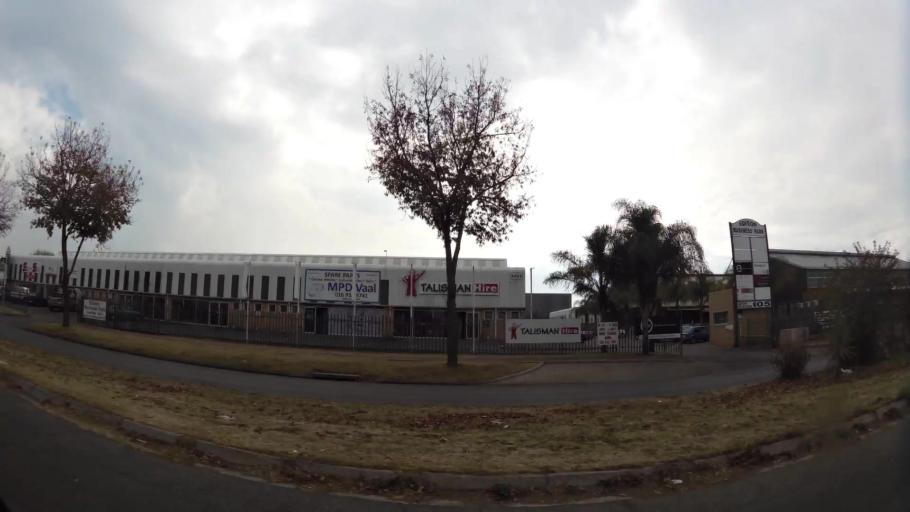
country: ZA
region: Gauteng
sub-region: Sedibeng District Municipality
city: Vanderbijlpark
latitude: -26.7057
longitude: 27.8510
